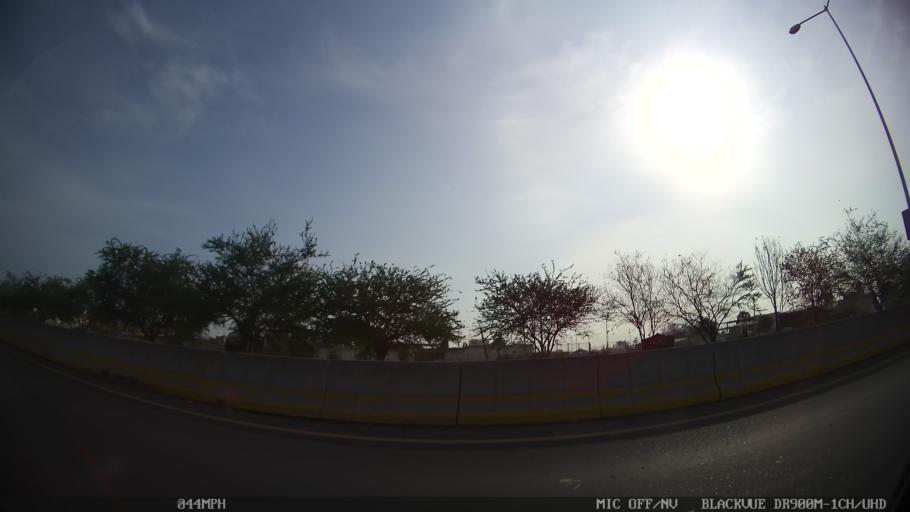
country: MX
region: Jalisco
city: Coyula
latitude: 20.6713
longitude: -103.2263
